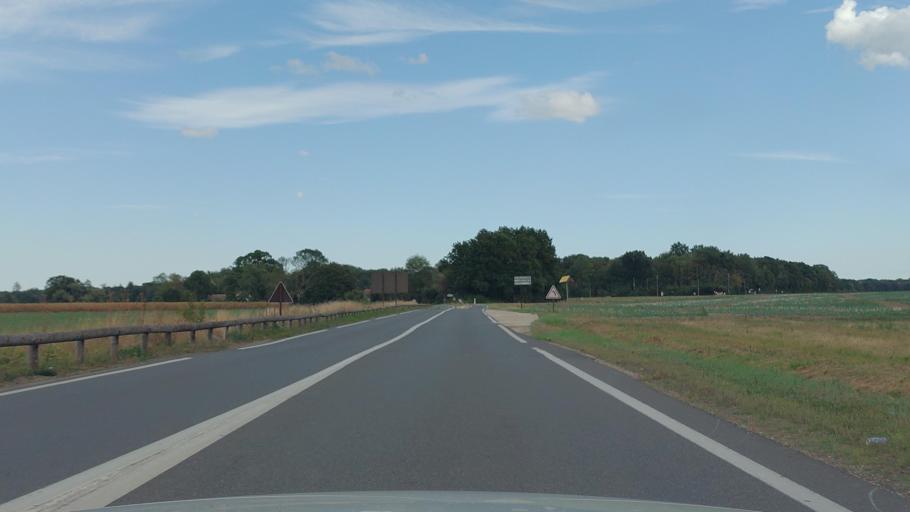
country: FR
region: Ile-de-France
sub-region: Departement de Seine-et-Marne
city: Le Chatelet-en-Brie
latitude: 48.5436
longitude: 2.7998
